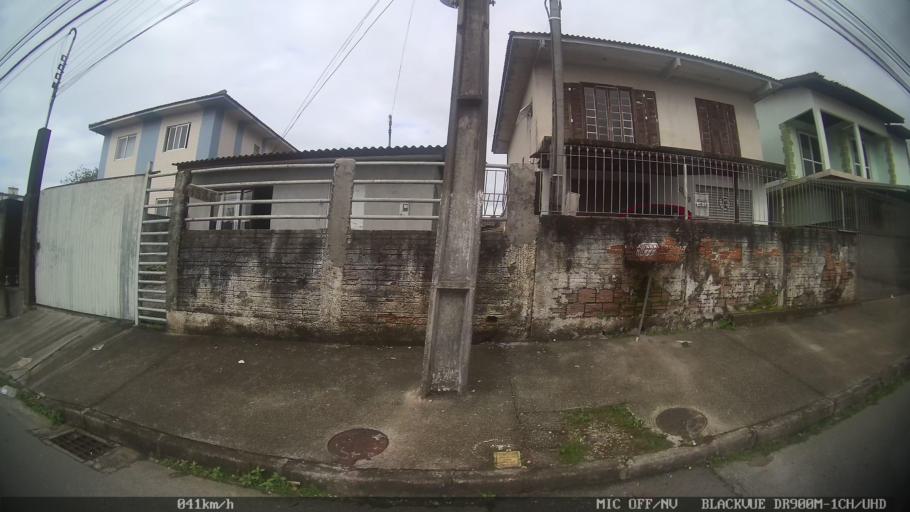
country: BR
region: Santa Catarina
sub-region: Sao Jose
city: Campinas
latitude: -27.5704
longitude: -48.6279
